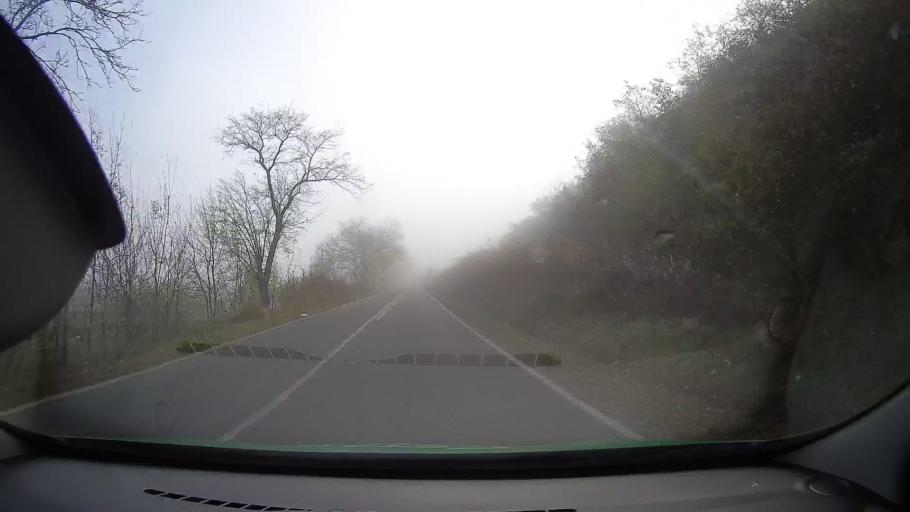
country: RO
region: Tulcea
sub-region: Comuna Nufaru
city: Malcoci
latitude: 45.1461
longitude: 28.8977
